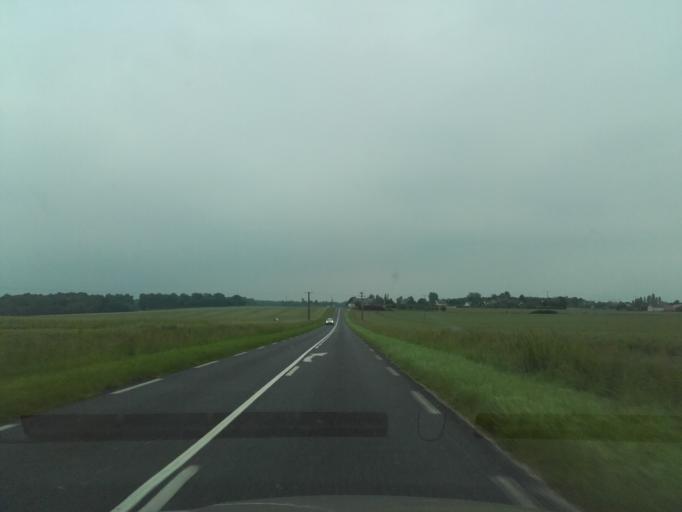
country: FR
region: Centre
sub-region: Departement d'Indre-et-Loire
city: Cerelles
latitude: 47.5214
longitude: 0.6944
